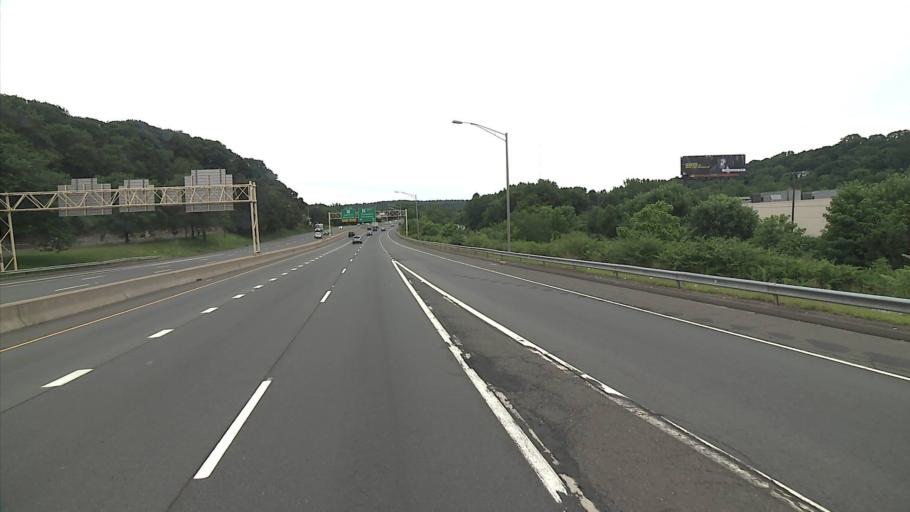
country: US
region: Connecticut
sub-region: New Haven County
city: Waterbury
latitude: 41.5604
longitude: -73.0568
